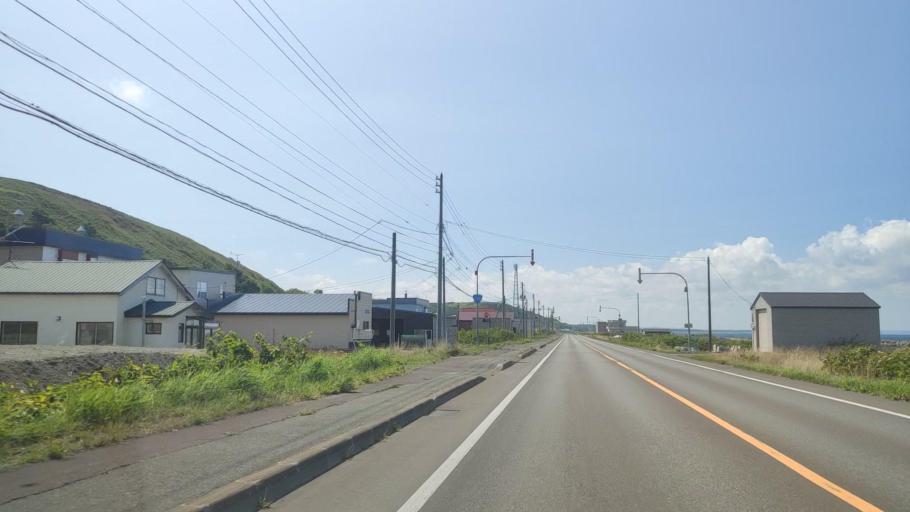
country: JP
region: Hokkaido
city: Makubetsu
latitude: 45.4583
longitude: 141.8776
